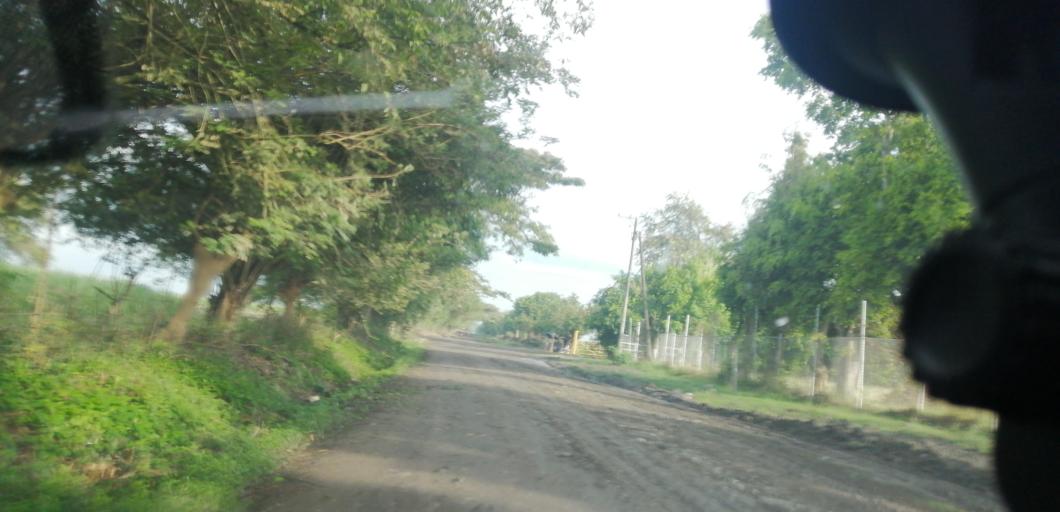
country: CO
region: Valle del Cauca
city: Palmira
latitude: 3.5432
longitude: -76.3606
